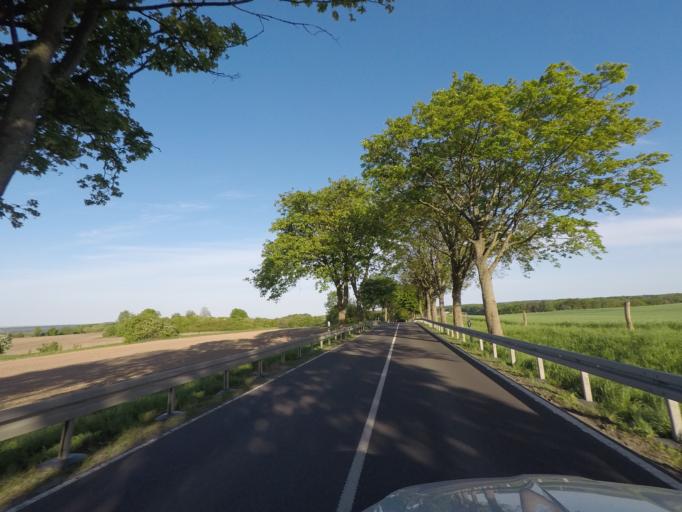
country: DE
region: Brandenburg
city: Hohenfinow
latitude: 52.8077
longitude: 13.9314
